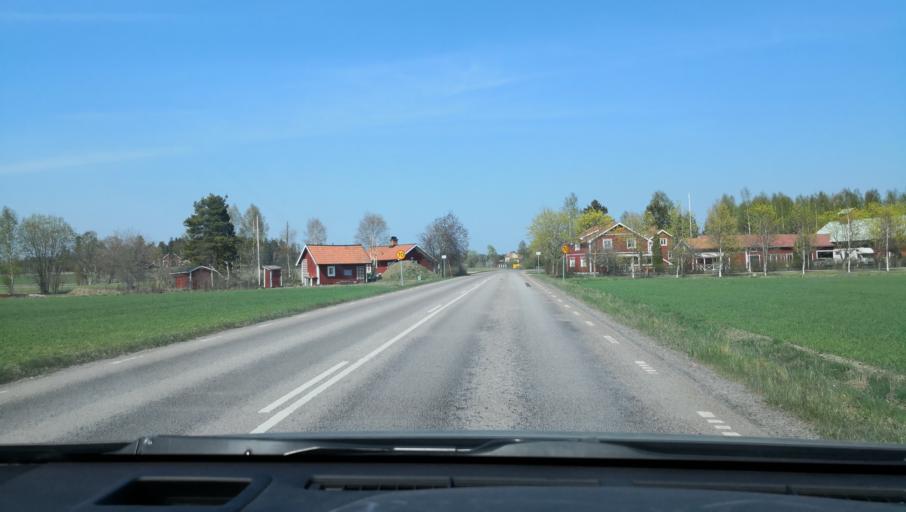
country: SE
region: Vaestmanland
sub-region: Sala Kommun
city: Sala
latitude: 59.9741
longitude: 16.6234
